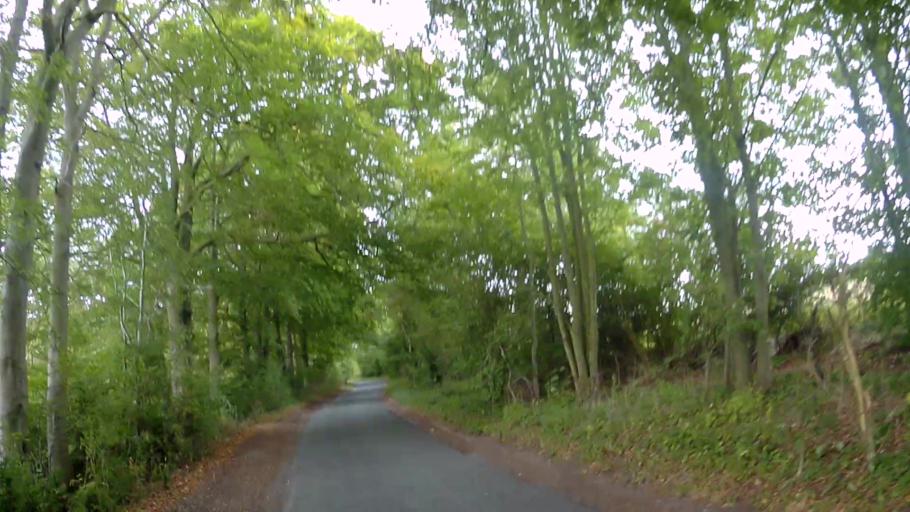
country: GB
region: England
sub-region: Hampshire
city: Overton
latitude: 51.1910
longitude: -1.2784
